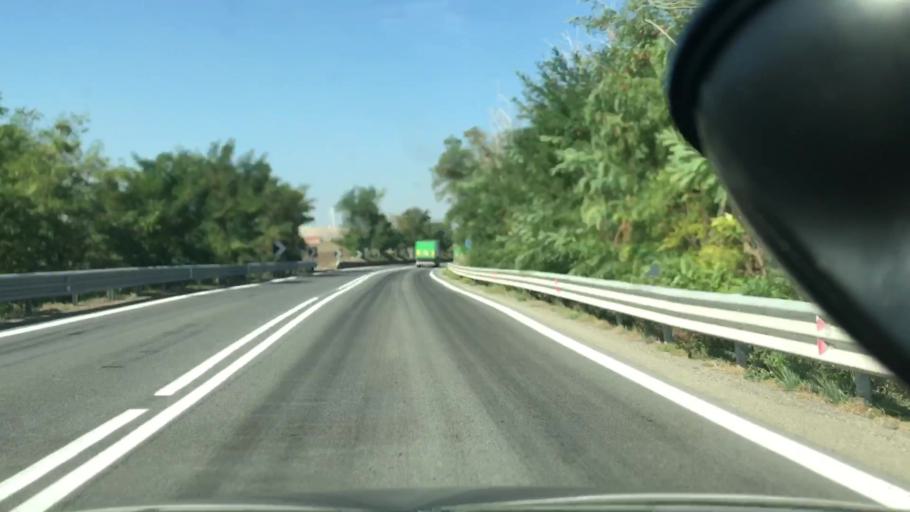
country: IT
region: Basilicate
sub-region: Provincia di Potenza
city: Zona 179
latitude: 41.0822
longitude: 15.6139
